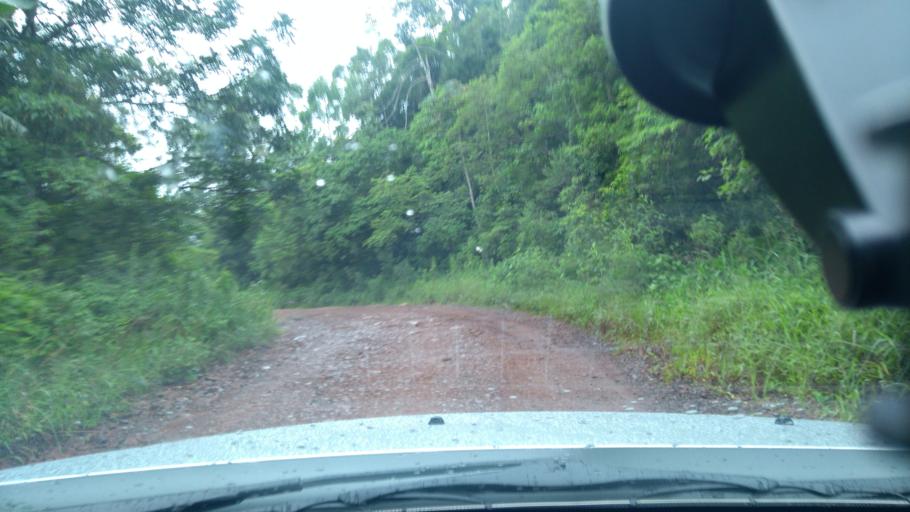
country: BR
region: Rio Grande do Sul
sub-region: Torres
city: Torres
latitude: -29.1800
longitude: -49.9873
